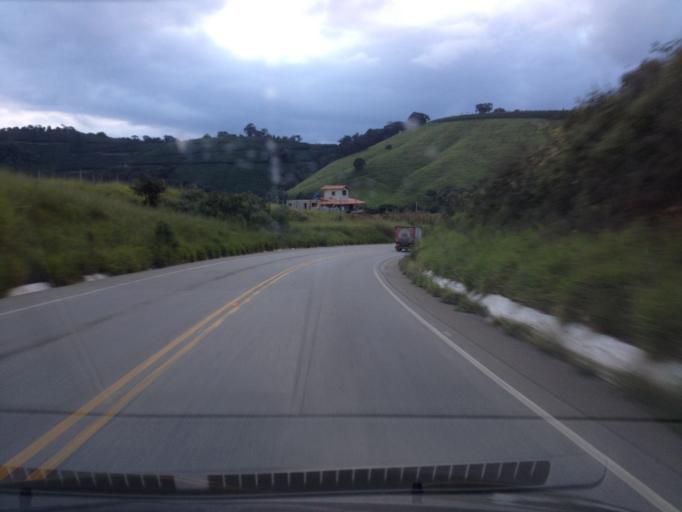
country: BR
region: Minas Gerais
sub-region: Sao Lourenco
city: Sao Lourenco
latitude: -22.0713
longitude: -45.0370
